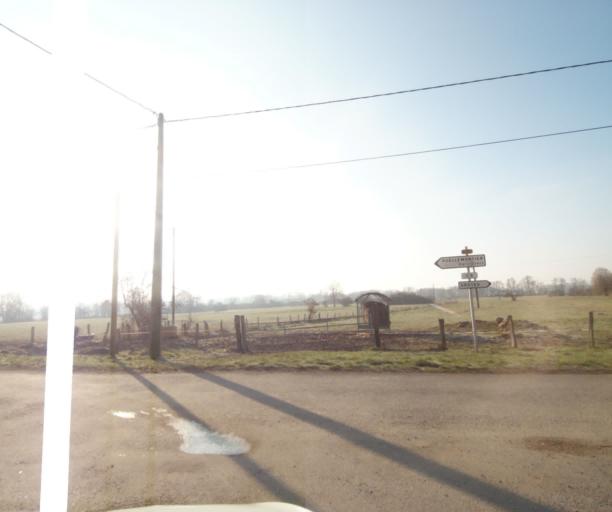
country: FR
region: Champagne-Ardenne
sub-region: Departement de la Haute-Marne
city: Montier-en-Der
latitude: 48.5034
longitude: 4.7276
